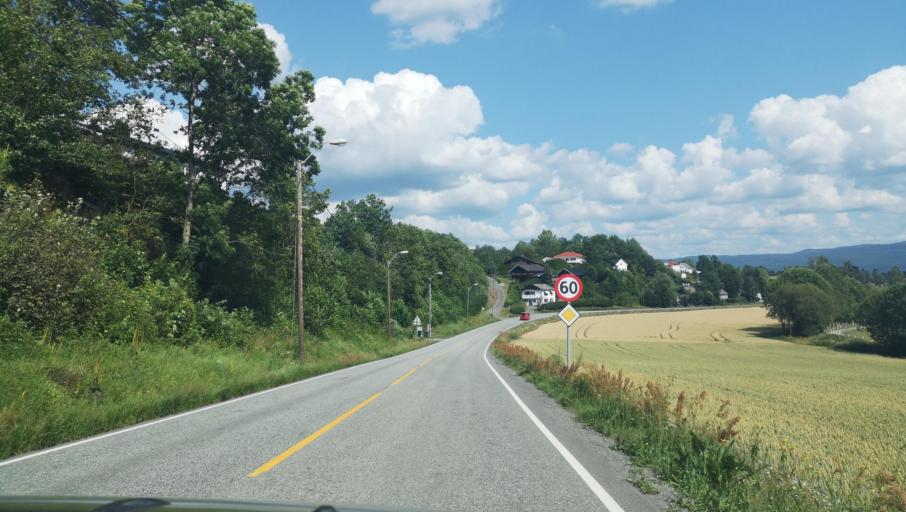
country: NO
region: Buskerud
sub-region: Ovre Eiker
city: Hokksund
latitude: 59.7342
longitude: 9.8495
